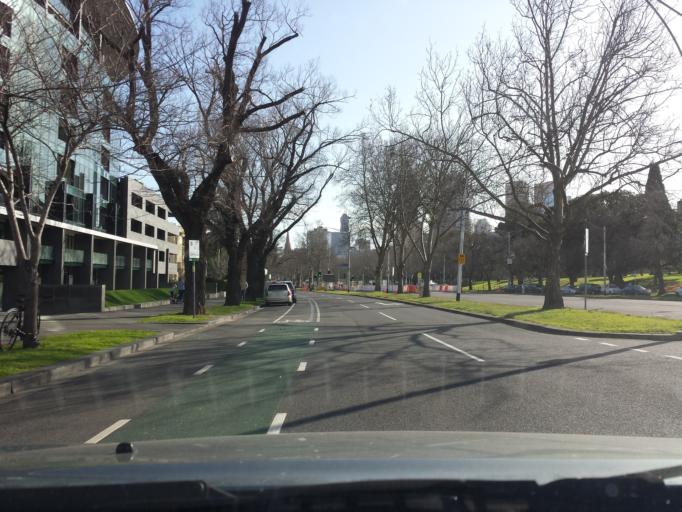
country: AU
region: Victoria
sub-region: Melbourne
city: Southbank
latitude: -37.8260
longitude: 144.9710
